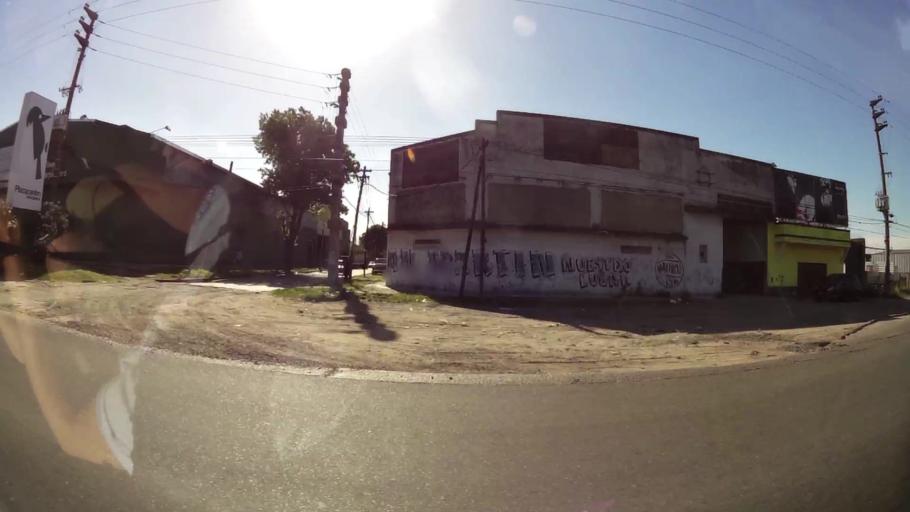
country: AR
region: Buenos Aires
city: Caseros
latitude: -34.5608
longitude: -58.5877
